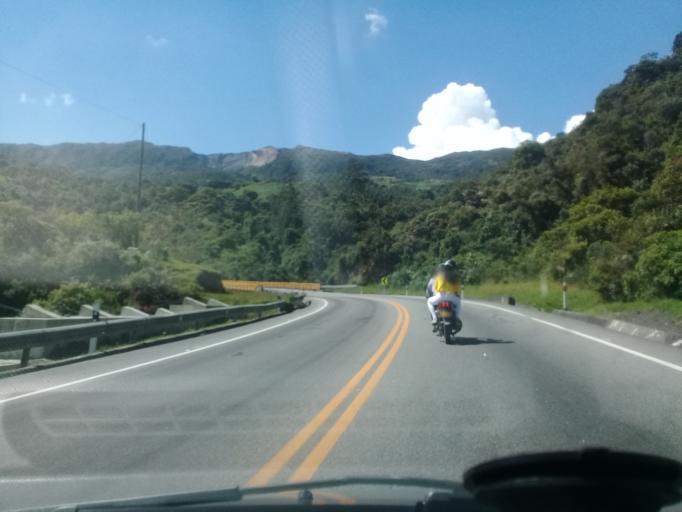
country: CO
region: Cundinamarca
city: Chipaque
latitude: 4.4539
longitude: -74.0620
